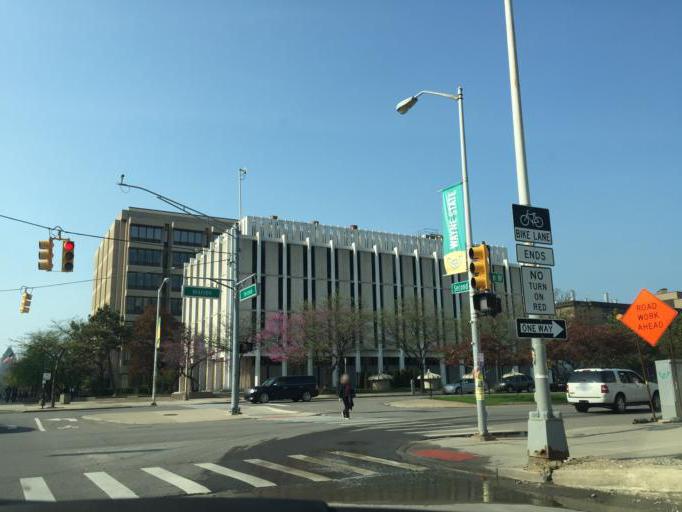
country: US
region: Michigan
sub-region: Wayne County
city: Detroit
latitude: 42.3550
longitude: -83.0688
